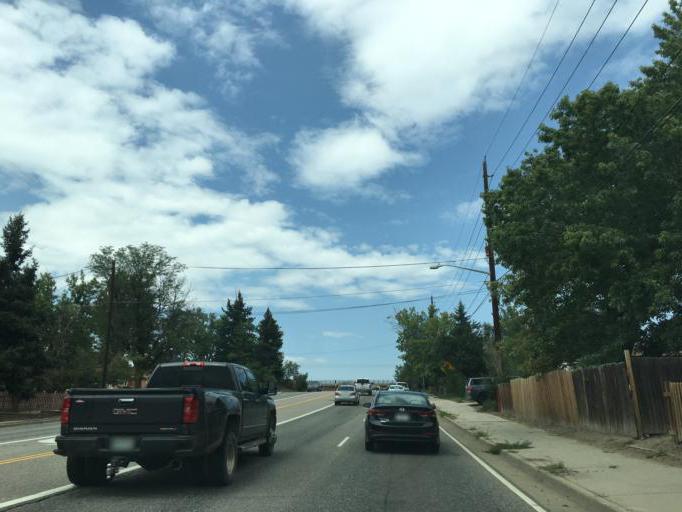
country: US
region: Colorado
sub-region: Jefferson County
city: Lakewood
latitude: 39.7344
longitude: -105.1095
